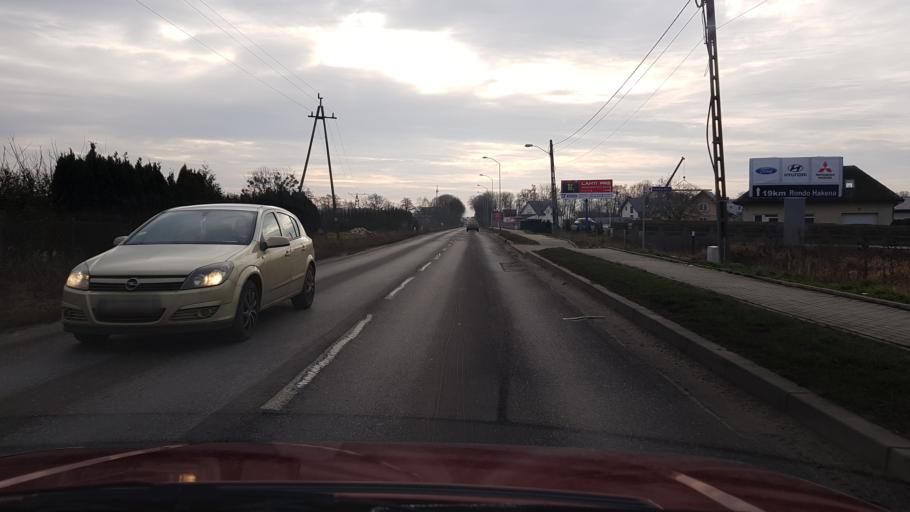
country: PL
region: West Pomeranian Voivodeship
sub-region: Powiat policki
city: Police
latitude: 53.5139
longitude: 14.5677
